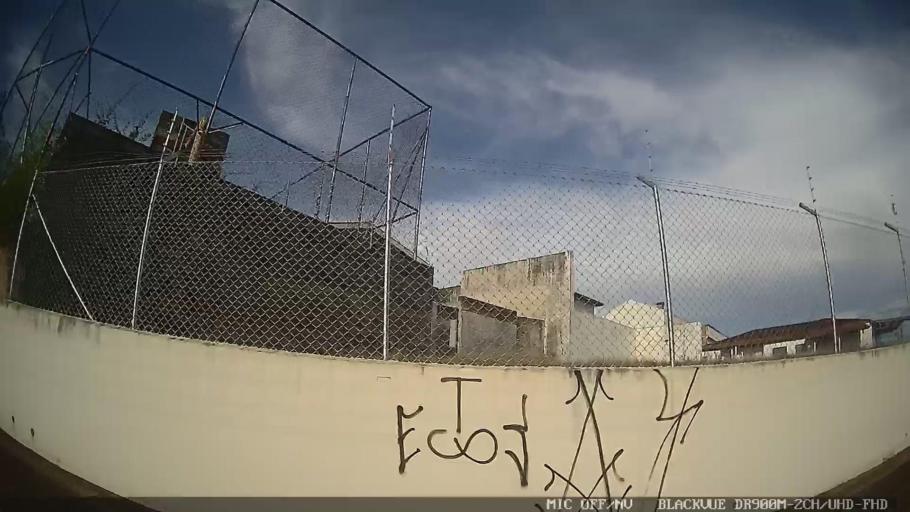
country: BR
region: Sao Paulo
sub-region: Tiete
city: Tiete
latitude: -23.1173
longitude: -47.7122
